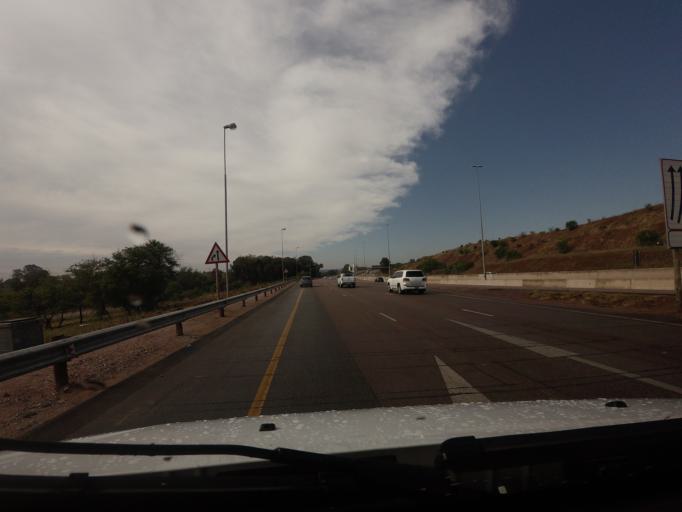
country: ZA
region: Gauteng
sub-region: City of Tshwane Metropolitan Municipality
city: Pretoria
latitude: -25.6884
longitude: 28.2829
